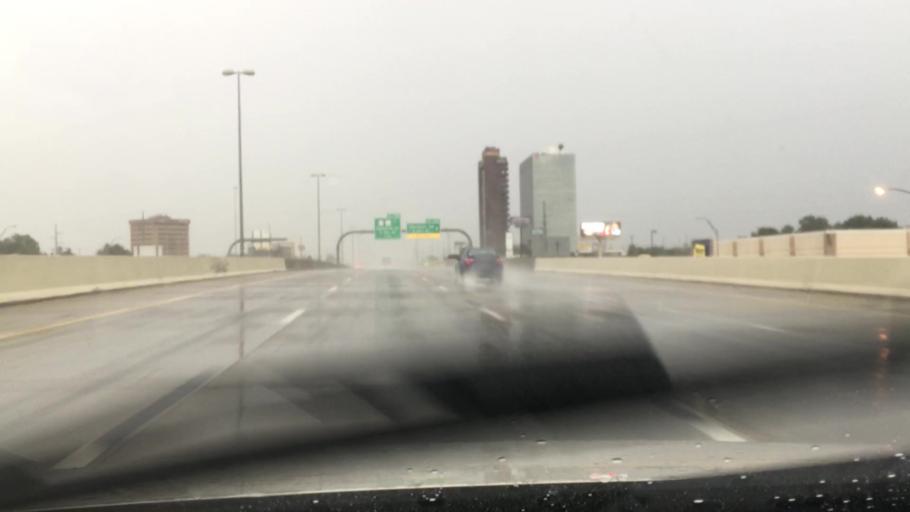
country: US
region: Oklahoma
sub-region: Tulsa County
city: Jenks
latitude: 36.0996
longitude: -95.9162
